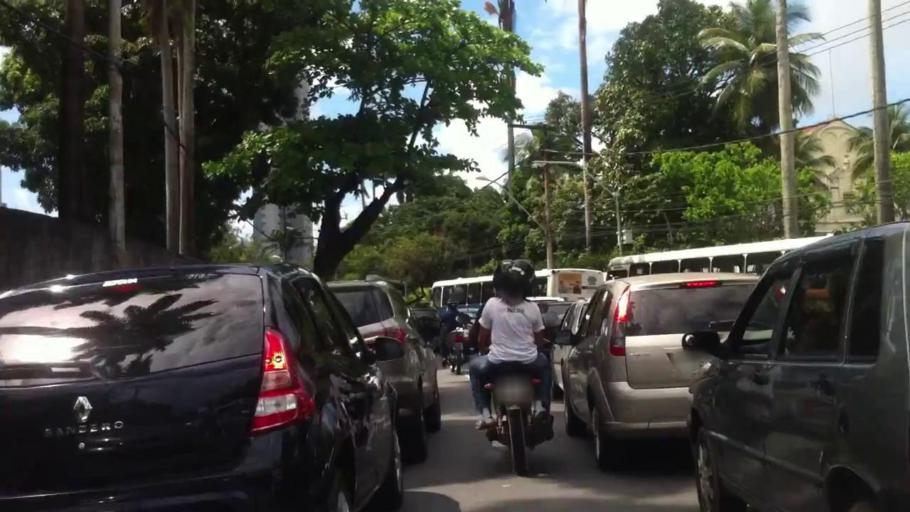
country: BR
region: Pernambuco
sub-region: Recife
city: Recife
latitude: -8.0420
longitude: -34.9028
